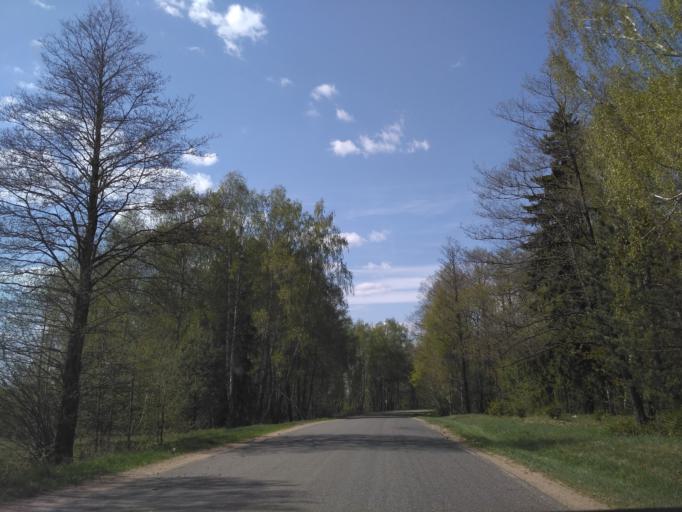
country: BY
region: Minsk
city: Narach
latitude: 54.9632
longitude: 26.6439
